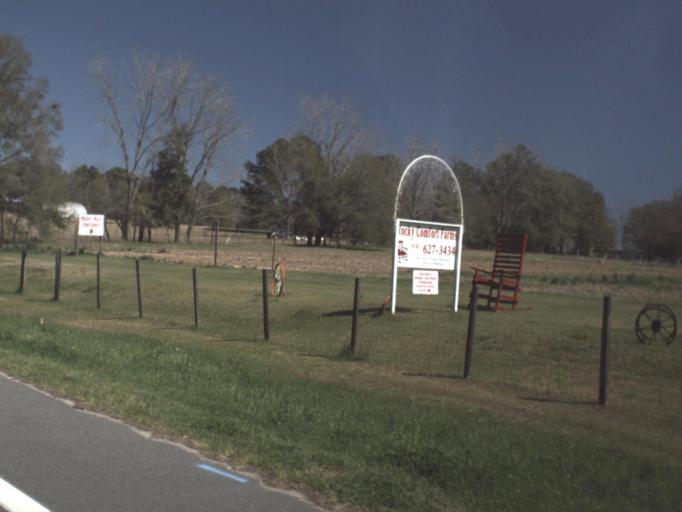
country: US
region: Florida
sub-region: Gadsden County
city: Quincy
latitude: 30.4976
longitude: -84.6091
